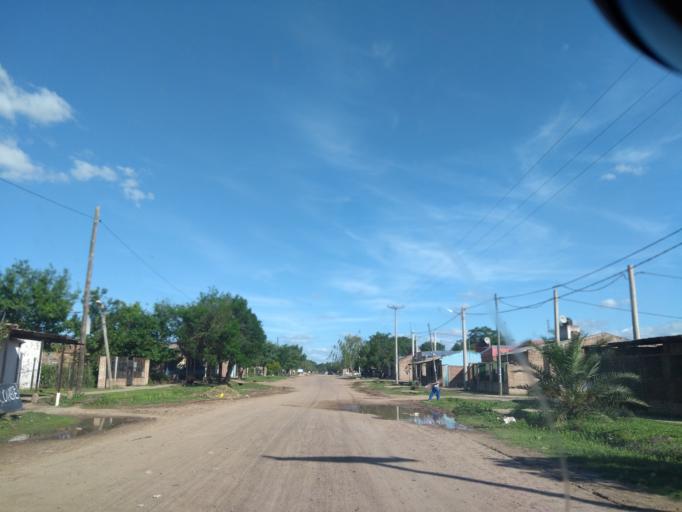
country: AR
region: Chaco
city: Resistencia
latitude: -27.4595
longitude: -58.9627
